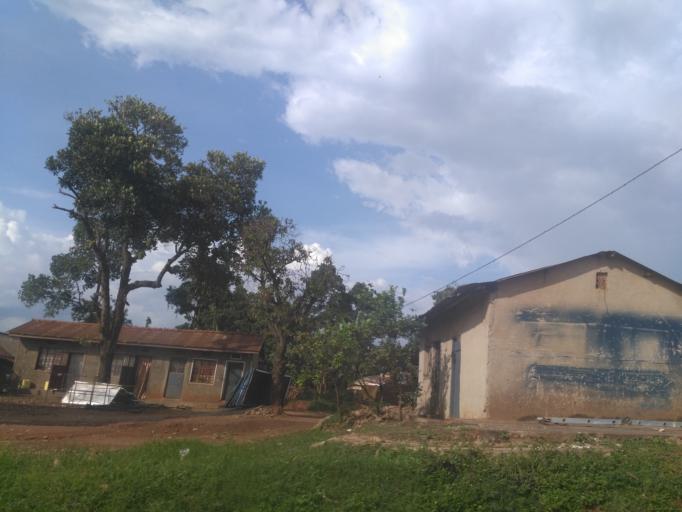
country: UG
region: Central Region
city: Kampala Central Division
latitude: 0.3602
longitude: 32.5764
